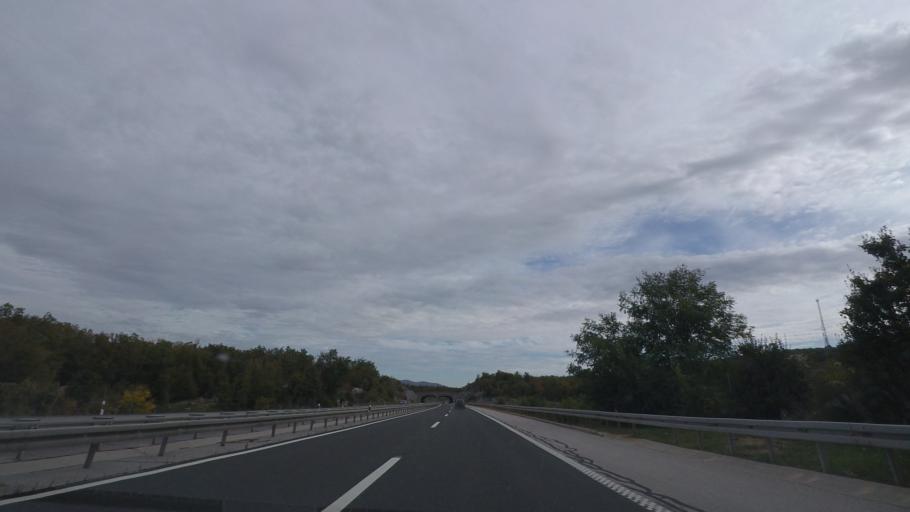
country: HR
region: Licko-Senjska
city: Gospic
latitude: 44.7031
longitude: 15.3933
